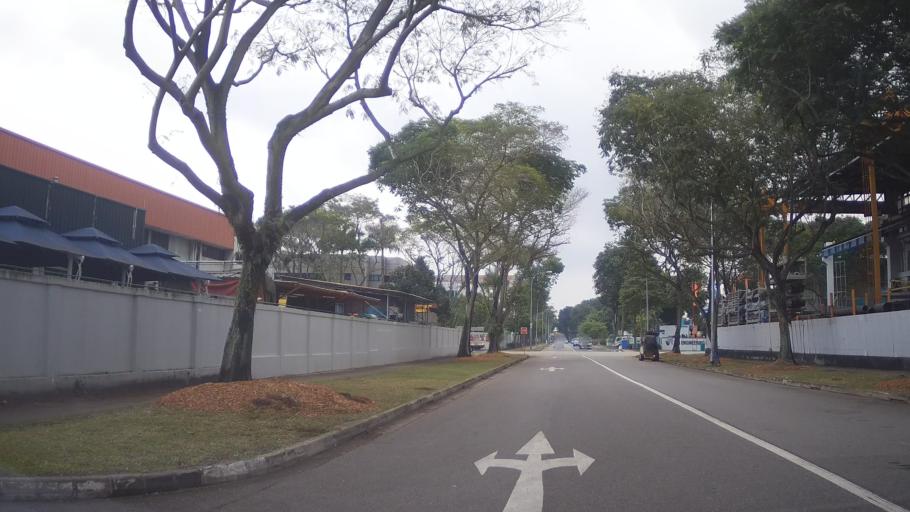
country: MY
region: Johor
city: Johor Bahru
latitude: 1.3322
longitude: 103.6926
